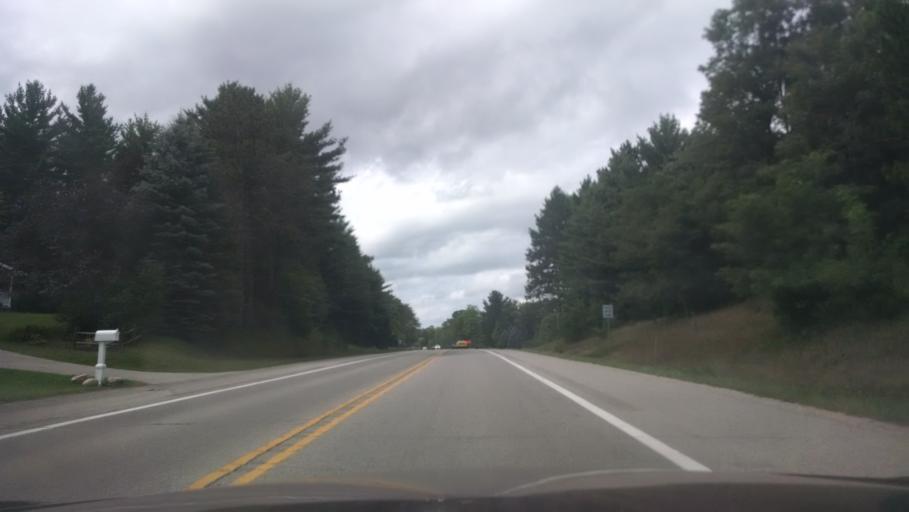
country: US
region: Michigan
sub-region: Wexford County
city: Cadillac
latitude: 44.1955
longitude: -85.3974
